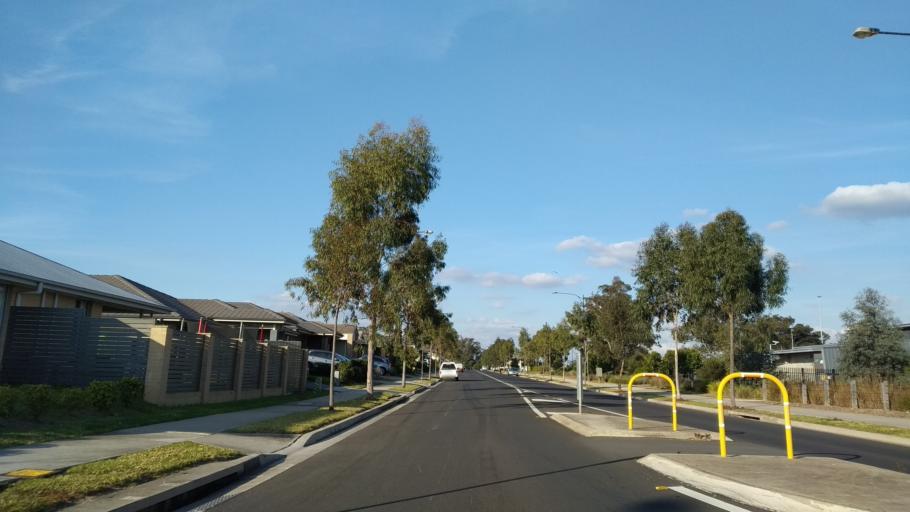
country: AU
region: New South Wales
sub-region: Penrith Municipality
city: Werrington Downs
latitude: -33.7229
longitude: 150.7278
